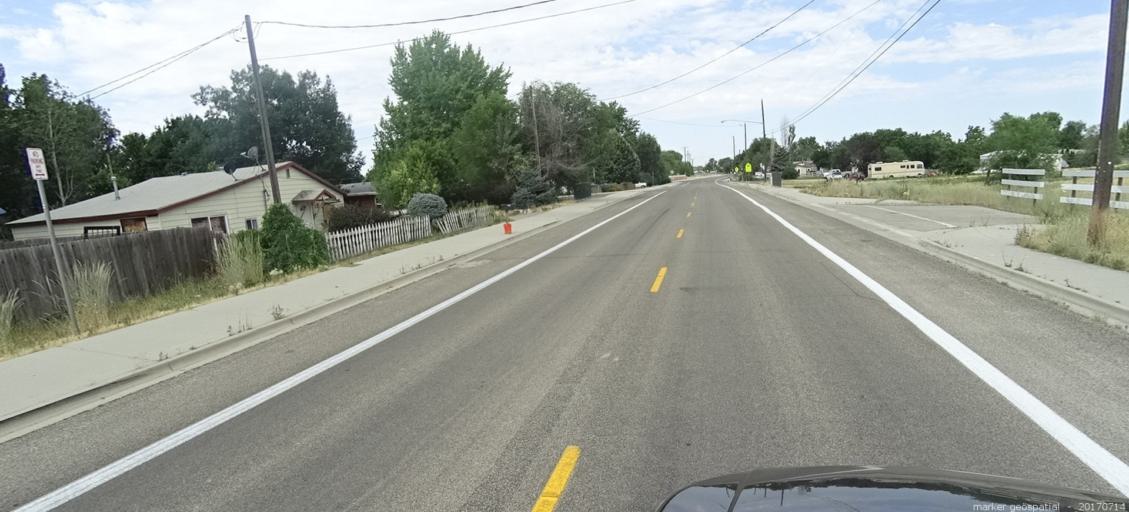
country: US
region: Idaho
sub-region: Ada County
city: Kuna
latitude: 43.4958
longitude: -116.4164
